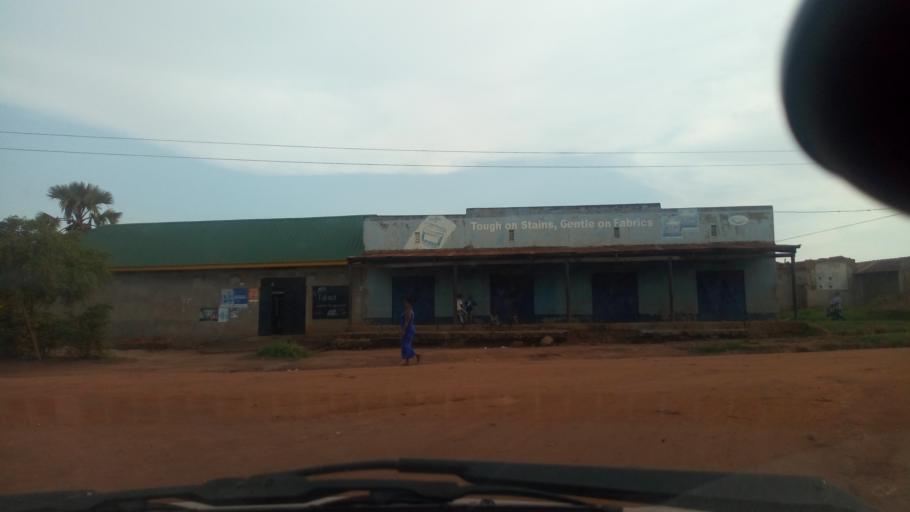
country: UG
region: Western Region
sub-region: Kiryandongo District
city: Kiryandongo
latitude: 1.8112
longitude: 32.0104
